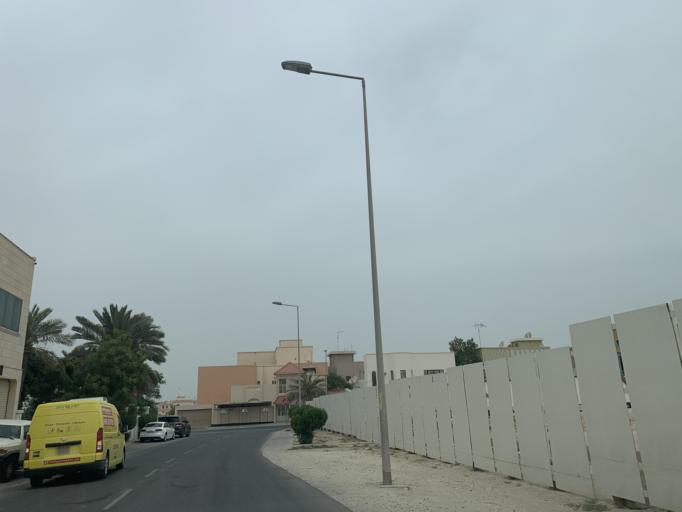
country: BH
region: Northern
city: Ar Rifa'
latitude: 26.1381
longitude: 50.5558
